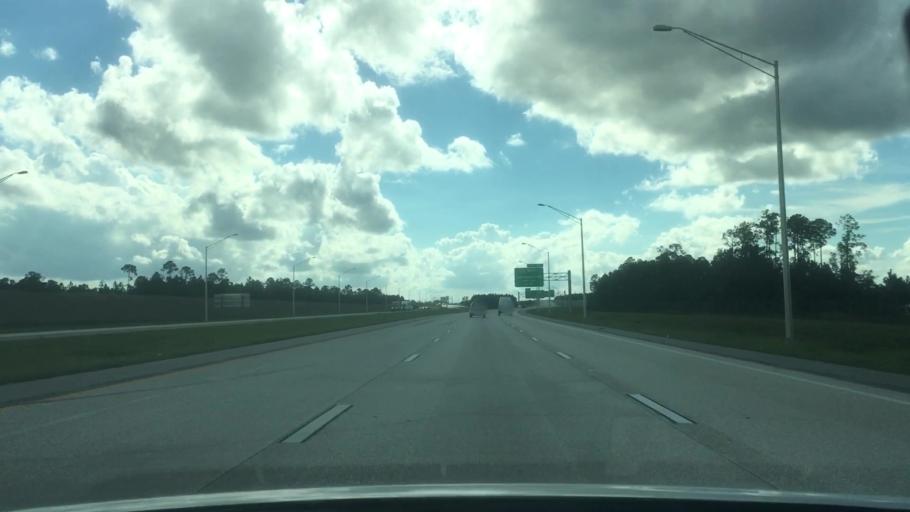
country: US
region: Florida
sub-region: Saint Johns County
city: Fruit Cove
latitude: 30.1271
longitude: -81.5115
